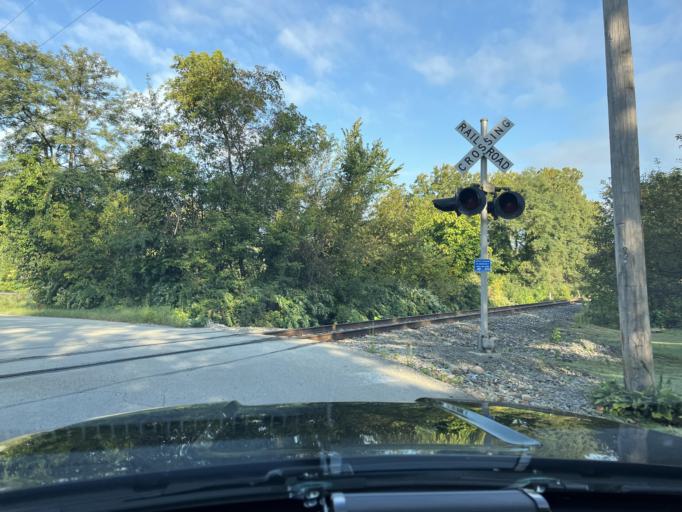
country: US
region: Pennsylvania
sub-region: Fayette County
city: Uniontown
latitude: 39.8909
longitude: -79.7192
